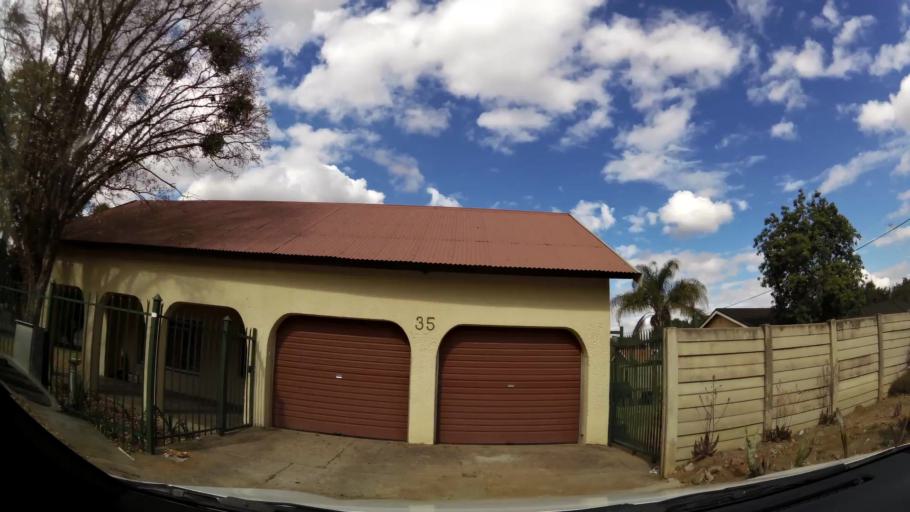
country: ZA
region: Limpopo
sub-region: Waterberg District Municipality
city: Modimolle
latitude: -24.7061
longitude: 28.4070
